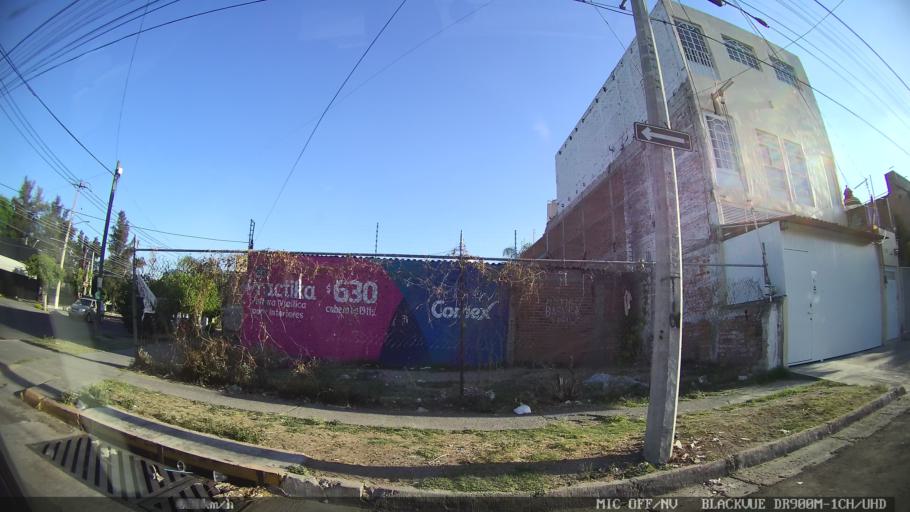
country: MX
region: Jalisco
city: Tlaquepaque
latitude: 20.6987
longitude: -103.2966
